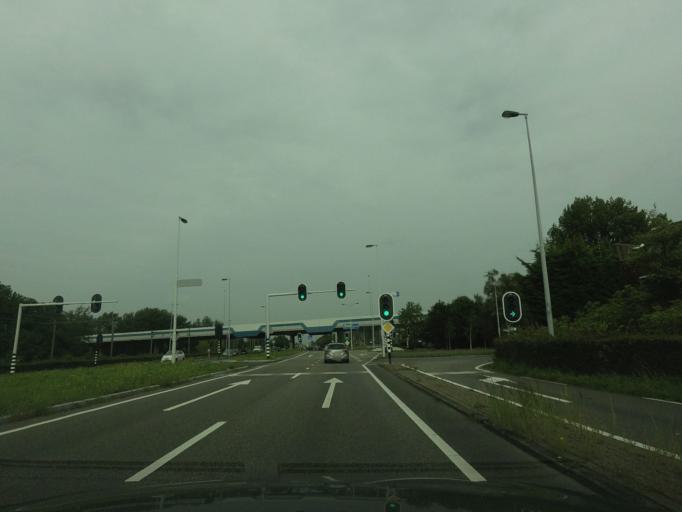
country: NL
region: North Holland
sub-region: Gemeente Zaanstad
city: Zaanstad
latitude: 52.4634
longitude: 4.8060
